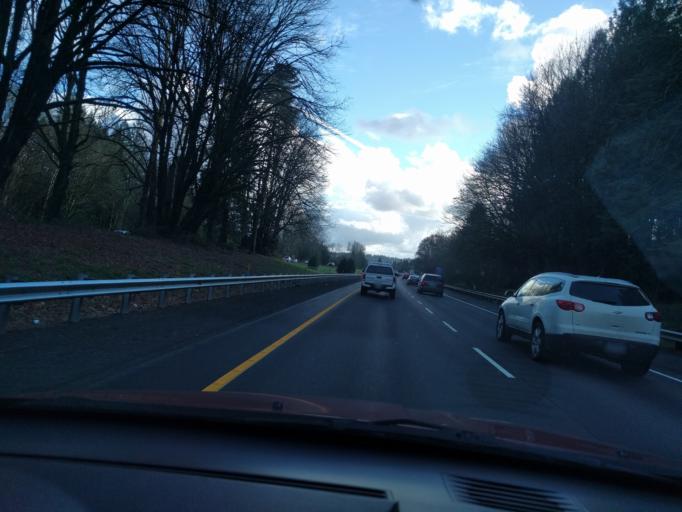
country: US
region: Oregon
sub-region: Clackamas County
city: West Linn
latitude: 45.3577
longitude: -122.6662
